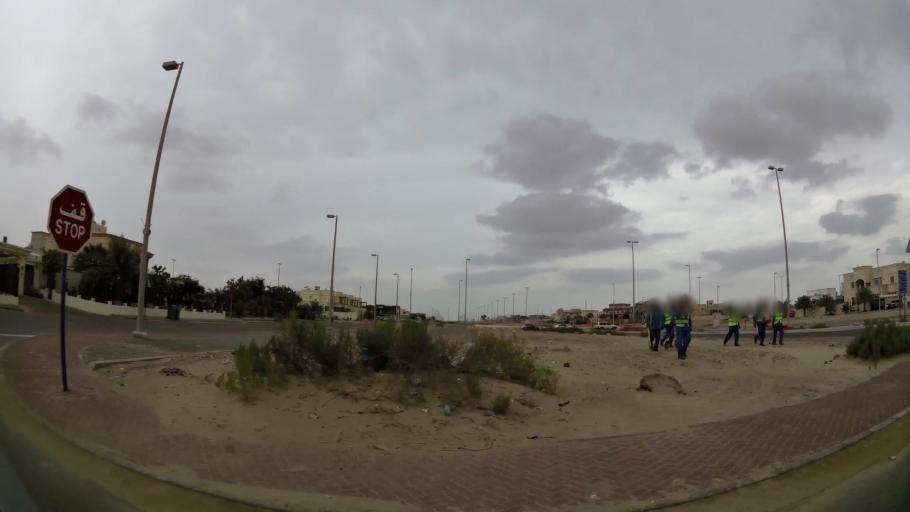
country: AE
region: Abu Dhabi
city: Abu Dhabi
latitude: 24.3753
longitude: 54.6454
